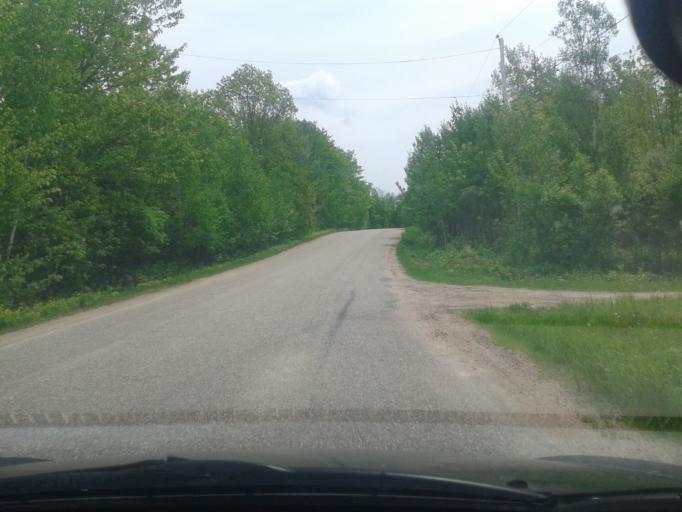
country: CA
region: Ontario
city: Powassan
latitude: 46.1852
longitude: -79.2221
